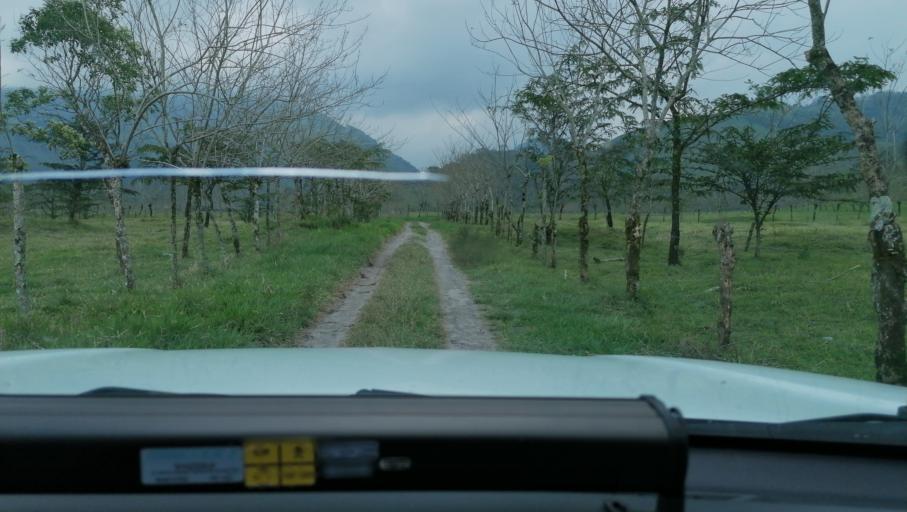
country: MX
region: Chiapas
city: Ixtacomitan
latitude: 17.3651
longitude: -93.1887
